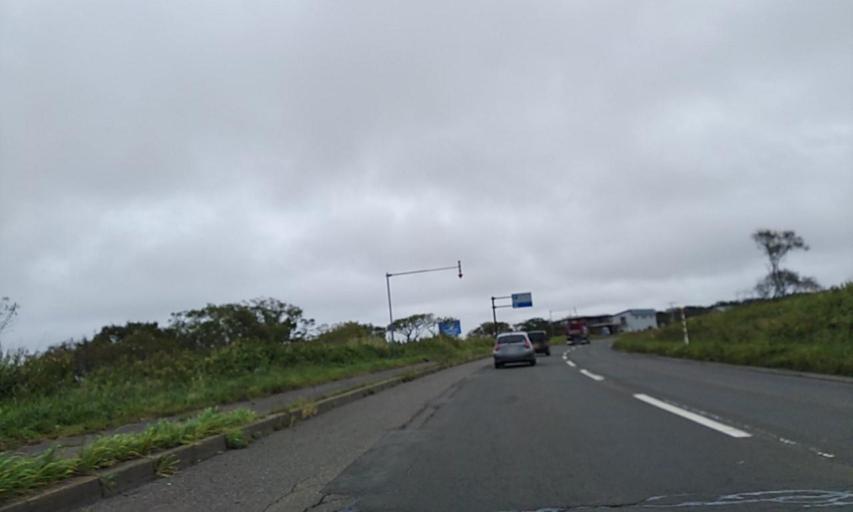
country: JP
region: Hokkaido
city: Nemuro
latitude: 43.2693
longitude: 145.4722
